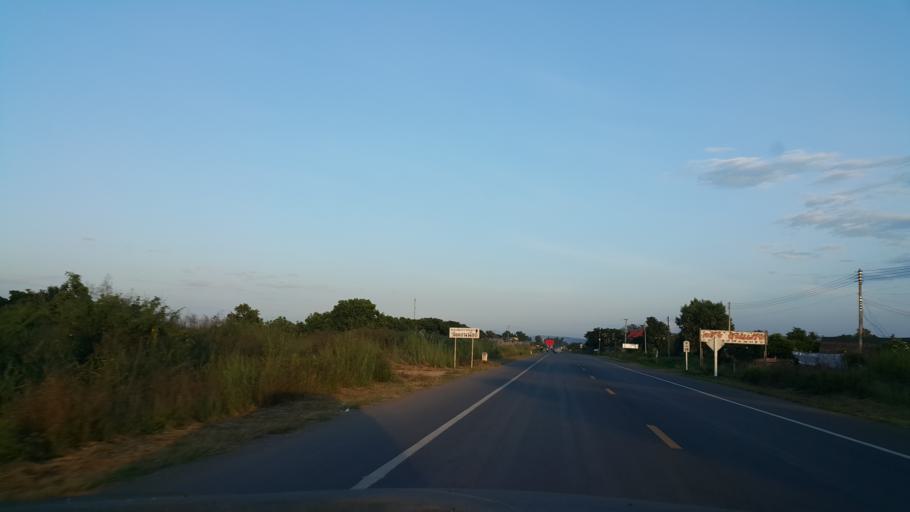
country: TH
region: Lamphun
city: Pa Sang
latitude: 18.4897
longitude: 98.9125
